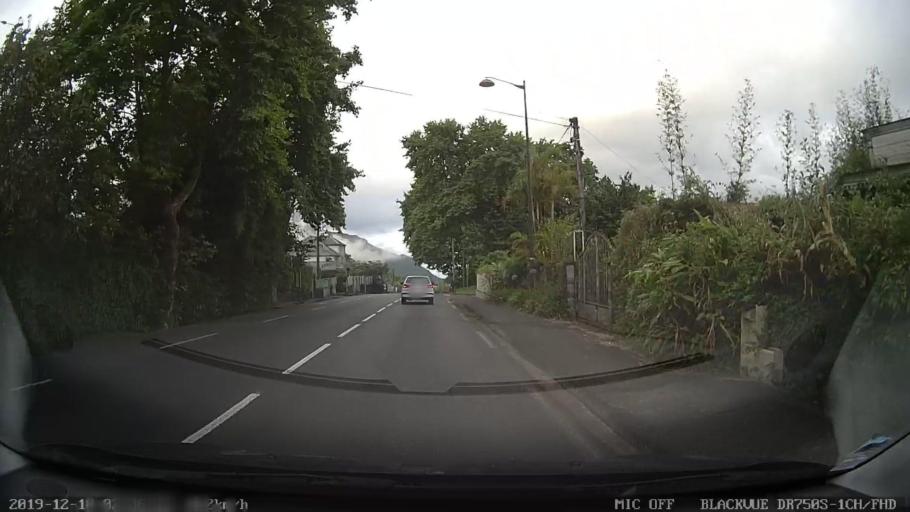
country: RE
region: Reunion
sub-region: Reunion
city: Salazie
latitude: -21.1411
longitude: 55.6220
